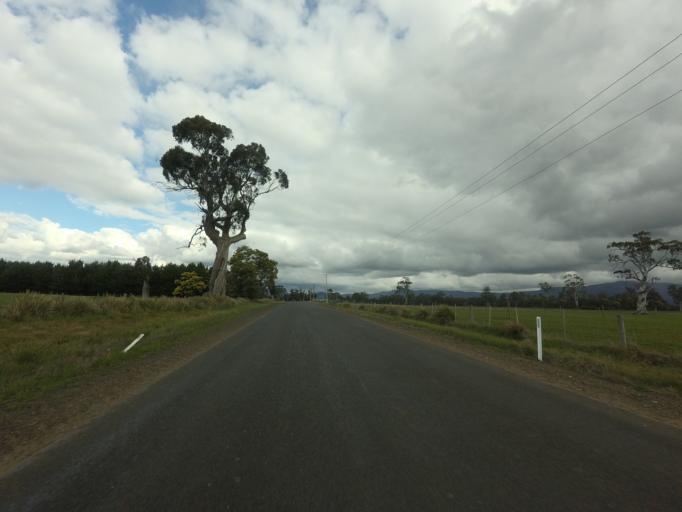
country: AU
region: Tasmania
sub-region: Northern Midlands
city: Longford
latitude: -41.7623
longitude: 147.0832
